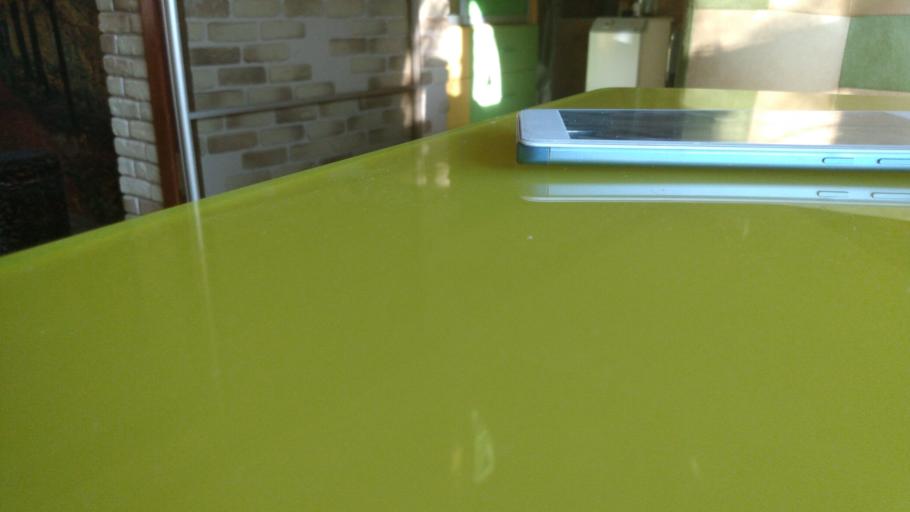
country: RU
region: Tverskaya
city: Vyshniy Volochek
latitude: 57.4519
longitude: 34.5717
